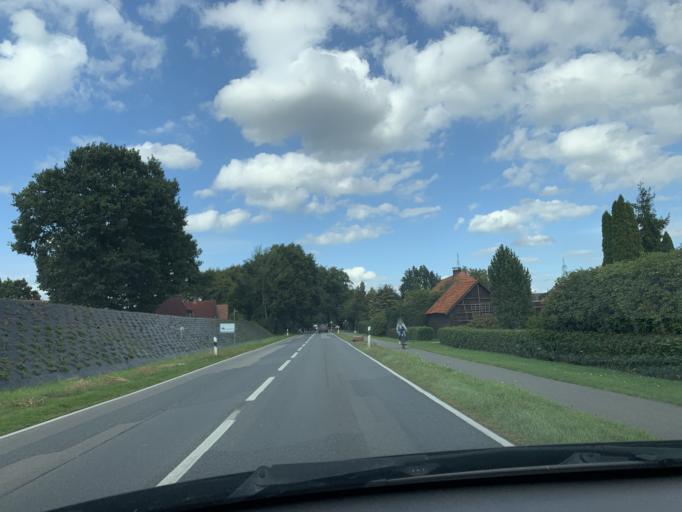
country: DE
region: Lower Saxony
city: Bad Zwischenahn
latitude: 53.1615
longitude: 7.9969
